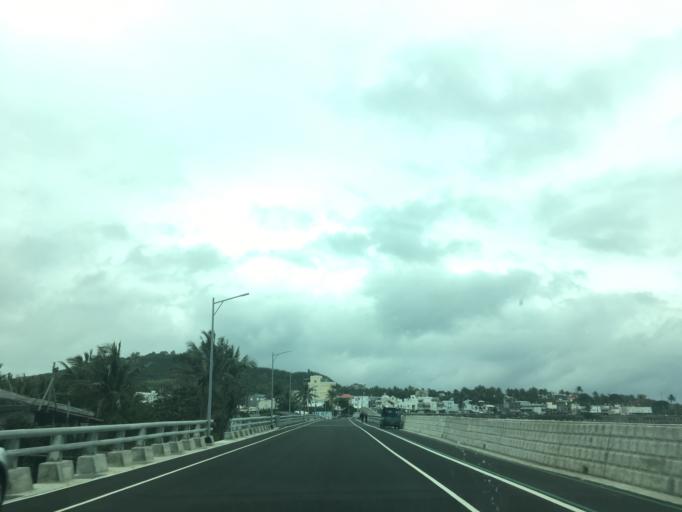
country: TW
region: Taiwan
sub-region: Taitung
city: Taitung
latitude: 22.7901
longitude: 121.1853
